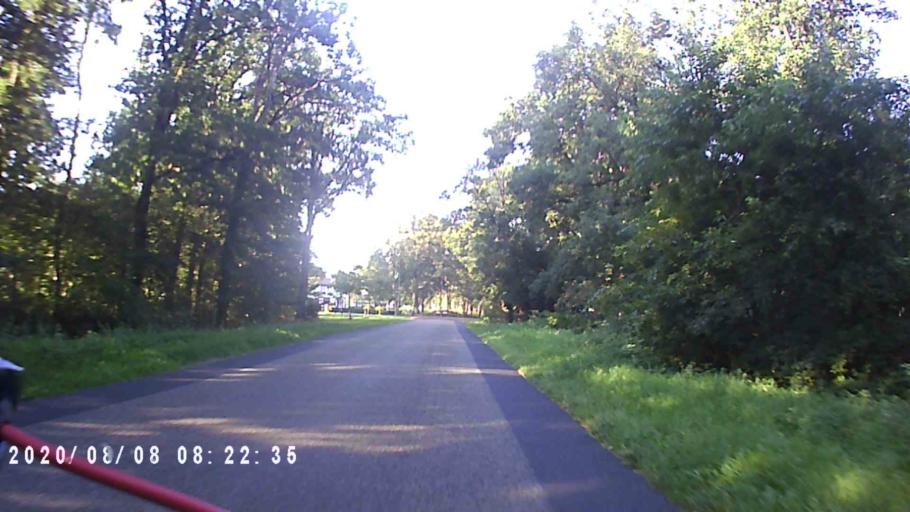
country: NL
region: Groningen
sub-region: Gemeente Leek
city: Leek
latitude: 53.0898
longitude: 6.3118
